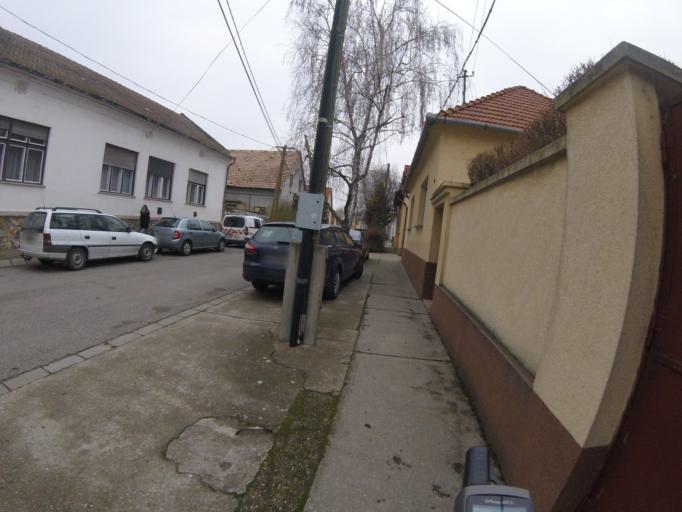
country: HU
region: Baranya
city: Mohacs
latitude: 45.9940
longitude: 18.6881
